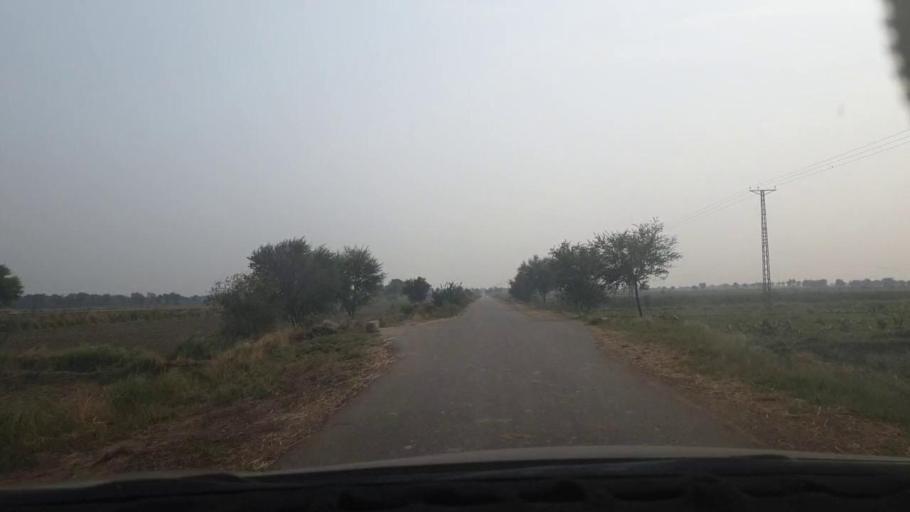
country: PK
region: Sindh
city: Jamshoro
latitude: 25.5182
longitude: 68.3145
